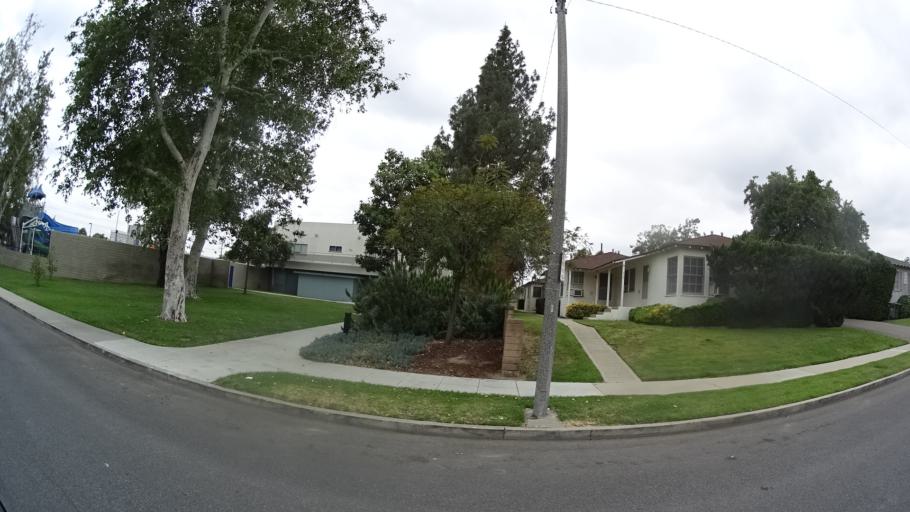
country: US
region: California
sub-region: Los Angeles County
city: Universal City
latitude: 34.1636
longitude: -118.3387
